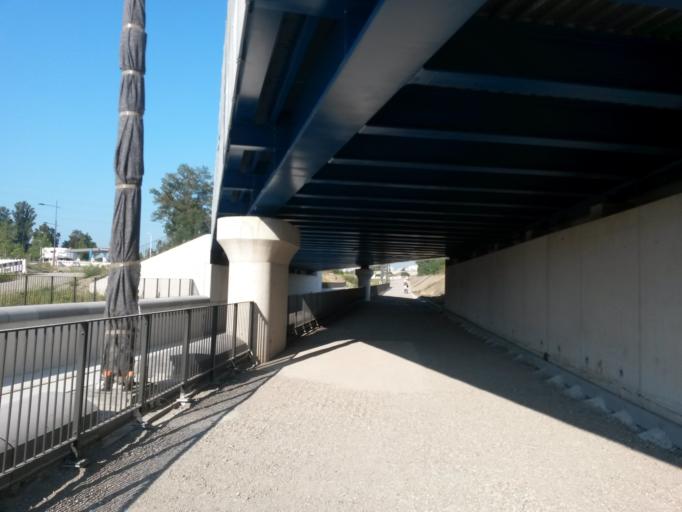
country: DE
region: Baden-Wuerttemberg
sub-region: Freiburg Region
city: Kehl
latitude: 48.5733
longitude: 7.7906
